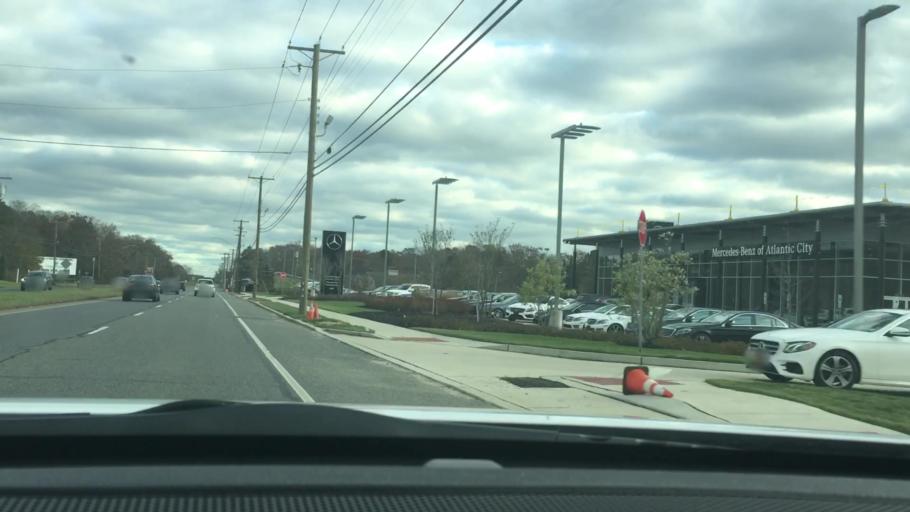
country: US
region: New Jersey
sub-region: Atlantic County
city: Northfield
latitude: 39.4169
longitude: -74.5801
